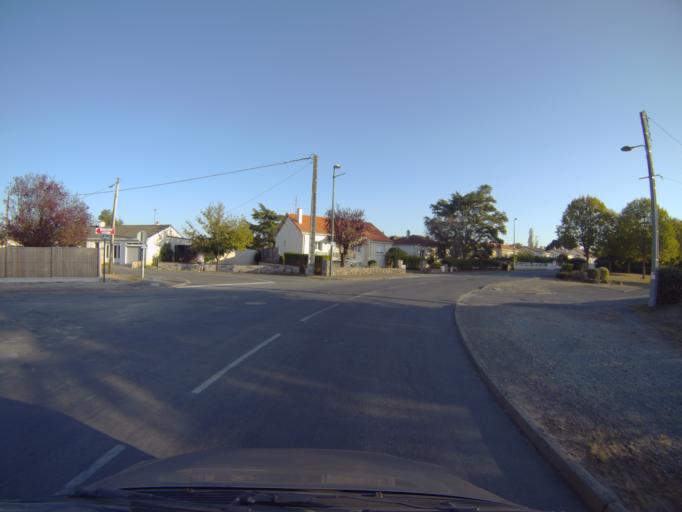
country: FR
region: Pays de la Loire
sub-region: Departement de la Vendee
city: Cugand
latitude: 47.0636
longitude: -1.2494
